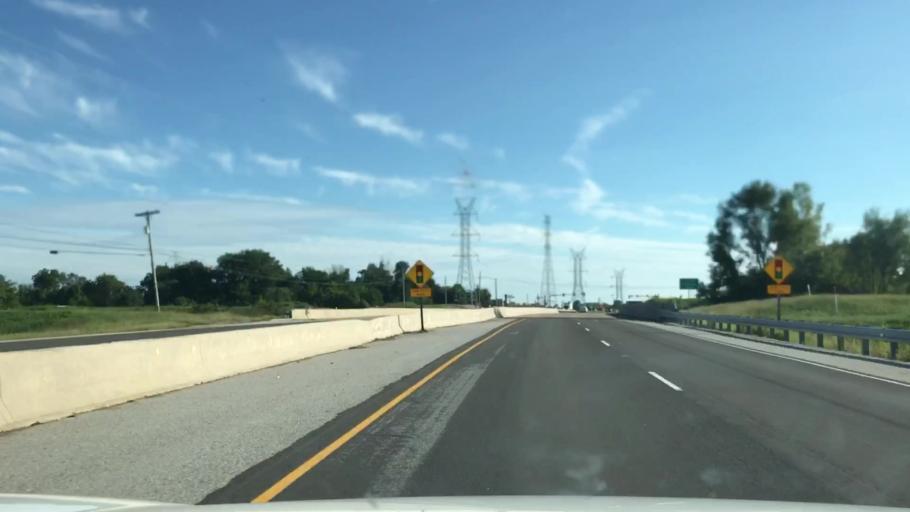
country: US
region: Illinois
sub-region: Madison County
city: Hartford
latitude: 38.8067
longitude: -90.0990
